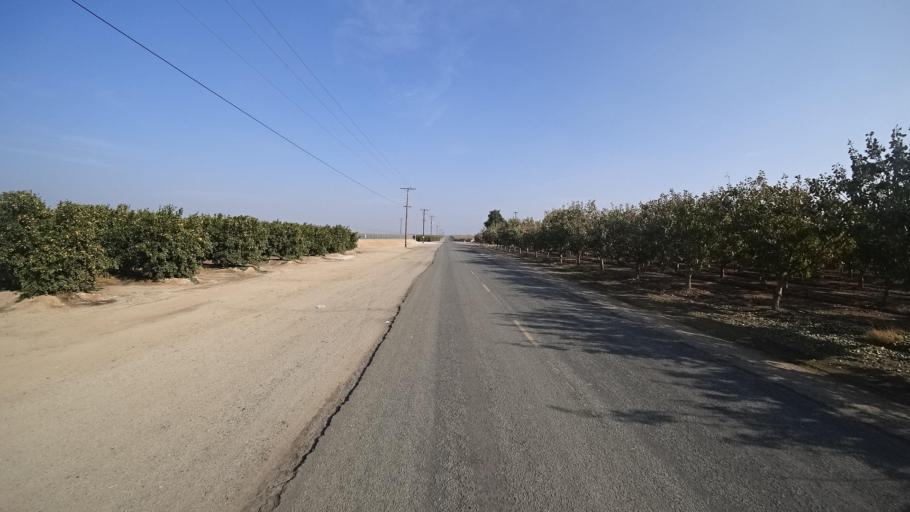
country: US
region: California
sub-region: Tulare County
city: Richgrove
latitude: 35.7908
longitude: -119.0821
